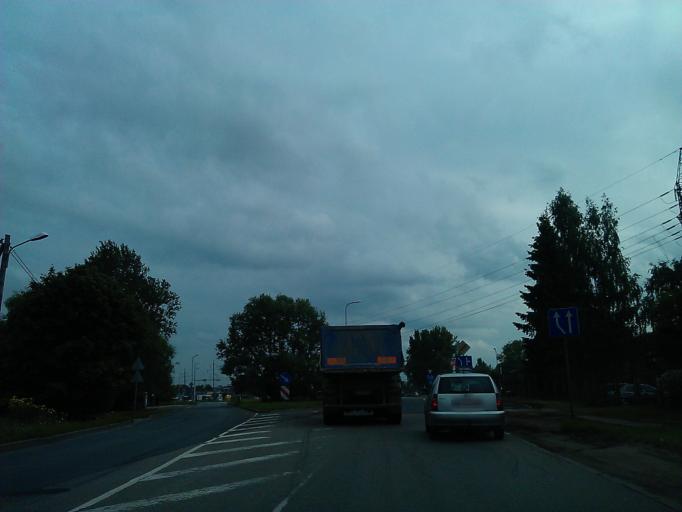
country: LV
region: Riga
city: Riga
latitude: 56.9472
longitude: 24.1639
